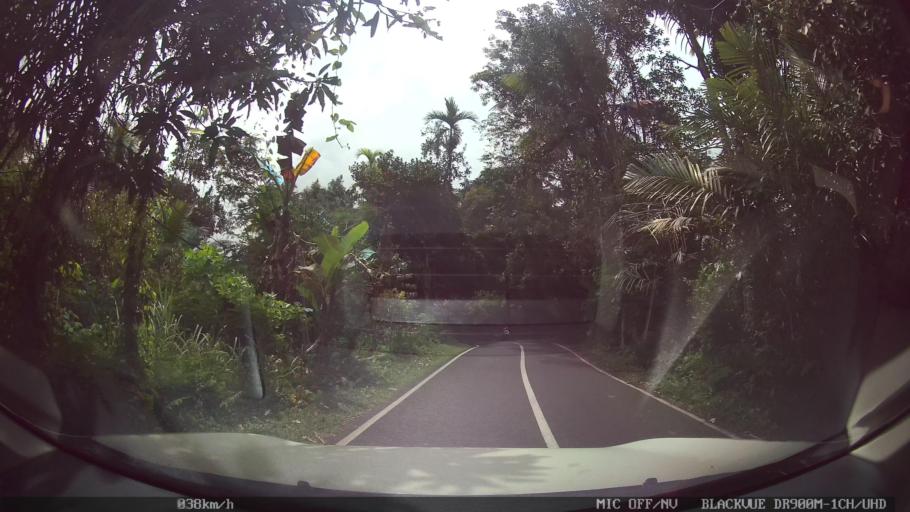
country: ID
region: Bali
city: Banjar Geriana Kangin
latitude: -8.4166
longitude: 115.4370
